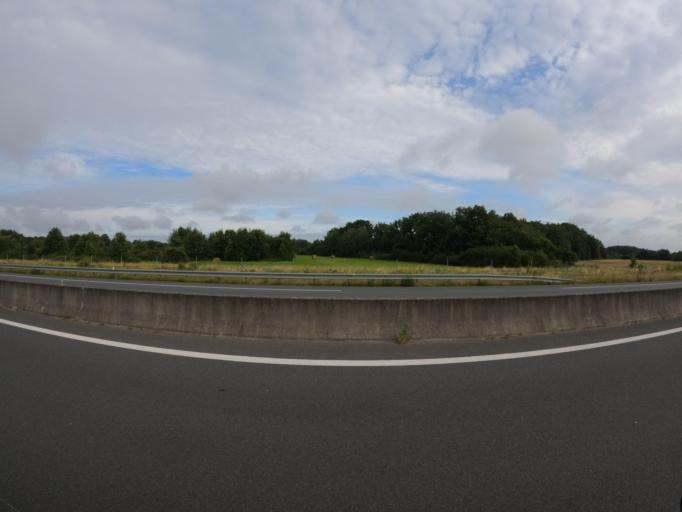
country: FR
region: Centre
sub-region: Departement d'Indre-et-Loire
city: Artannes-sur-Indre
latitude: 47.3069
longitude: 0.5789
